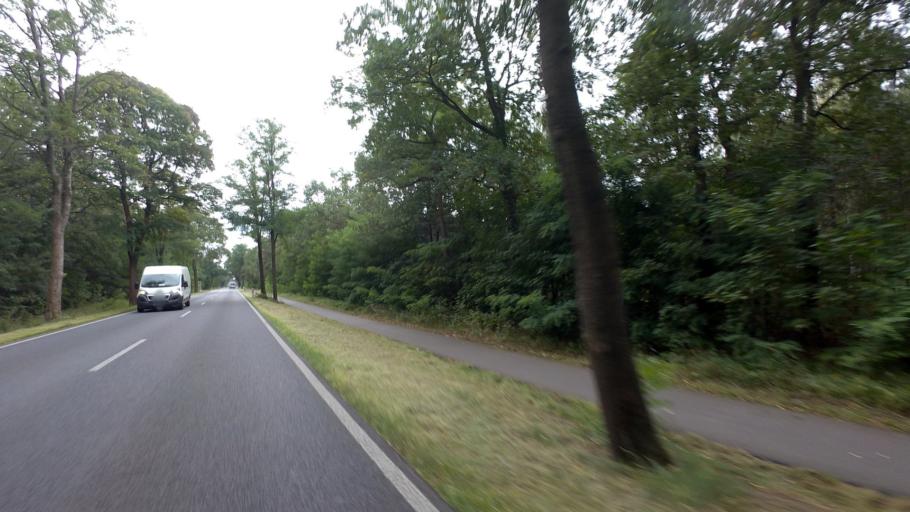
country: DE
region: Brandenburg
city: Baruth
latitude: 52.0721
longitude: 13.5045
